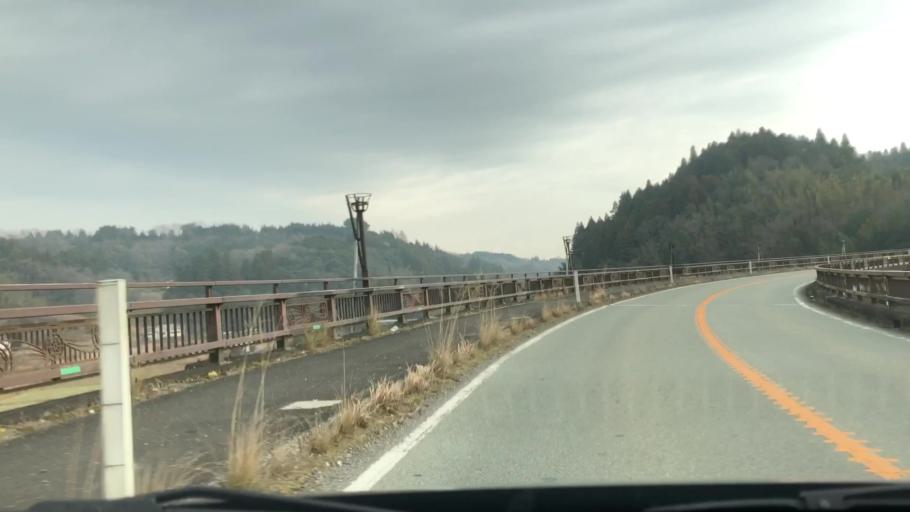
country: JP
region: Oita
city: Takedamachi
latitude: 32.9720
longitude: 131.5010
